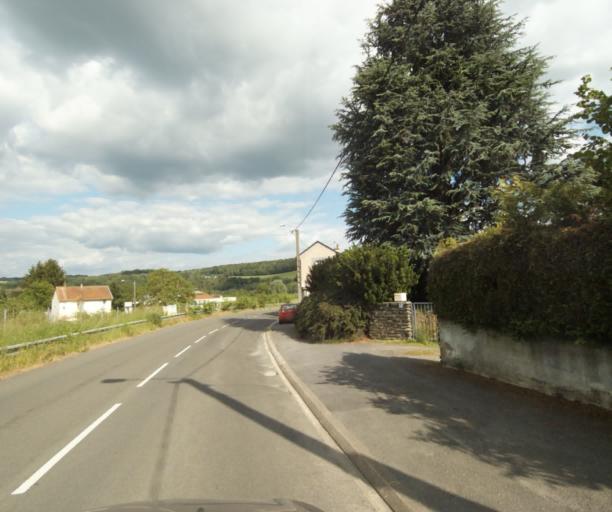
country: FR
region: Champagne-Ardenne
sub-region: Departement des Ardennes
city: Montcy-Notre-Dame
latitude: 49.7720
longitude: 4.7378
